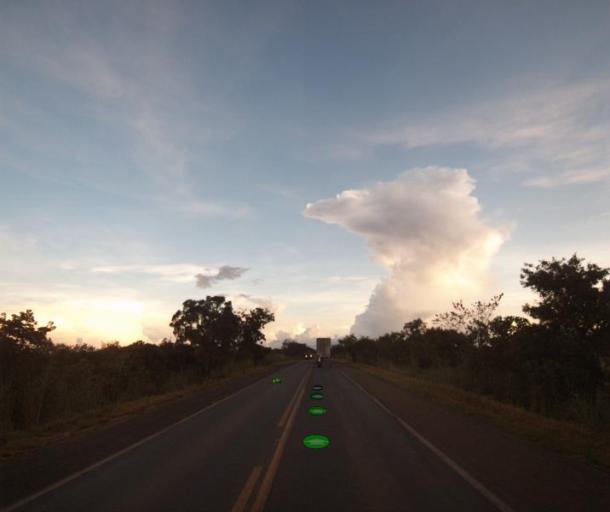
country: BR
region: Goias
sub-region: Uruacu
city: Uruacu
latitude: -14.4481
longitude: -49.1565
